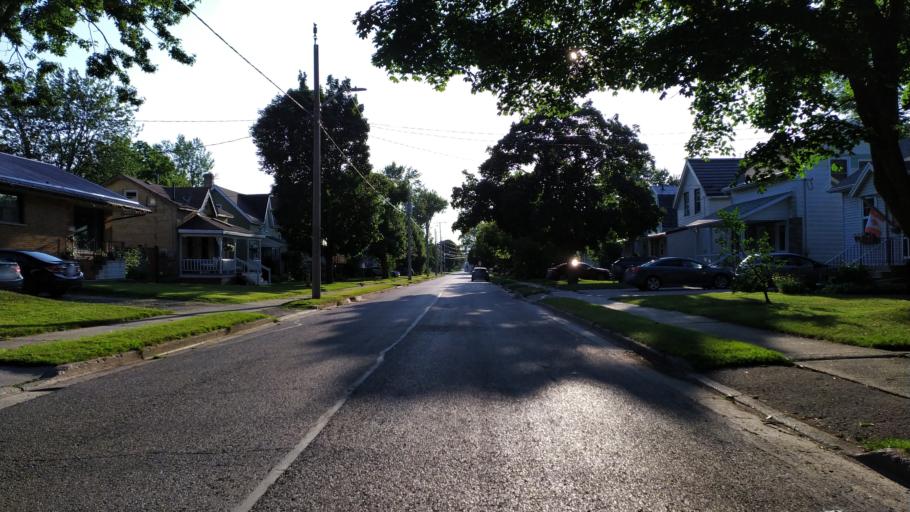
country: CA
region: Ontario
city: Stratford
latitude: 43.3693
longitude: -80.9611
